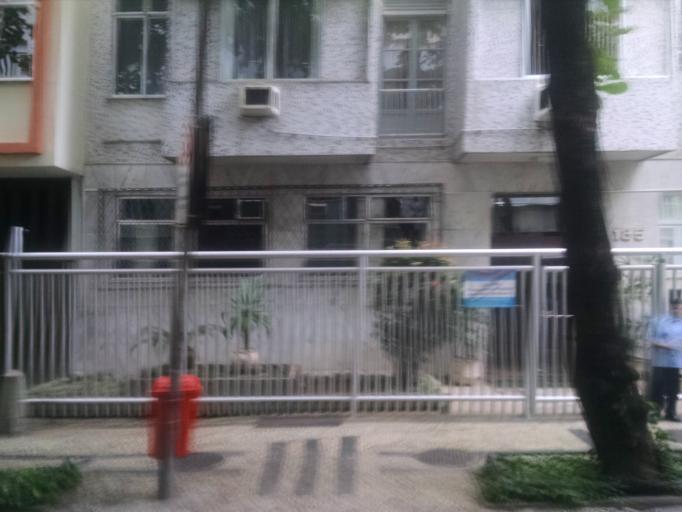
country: BR
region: Rio de Janeiro
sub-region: Rio De Janeiro
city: Rio de Janeiro
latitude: -22.9864
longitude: -43.1920
